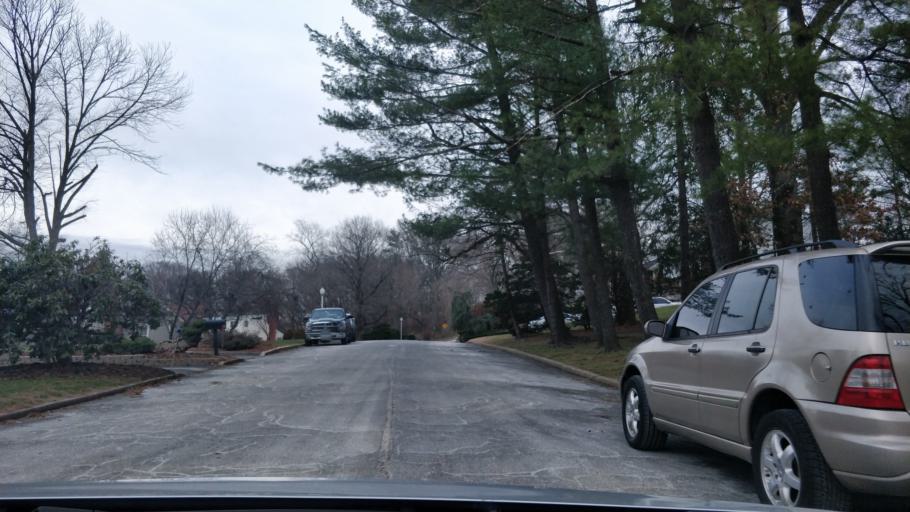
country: US
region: New York
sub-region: Nassau County
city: Glen Cove
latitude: 40.8731
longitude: -73.6381
